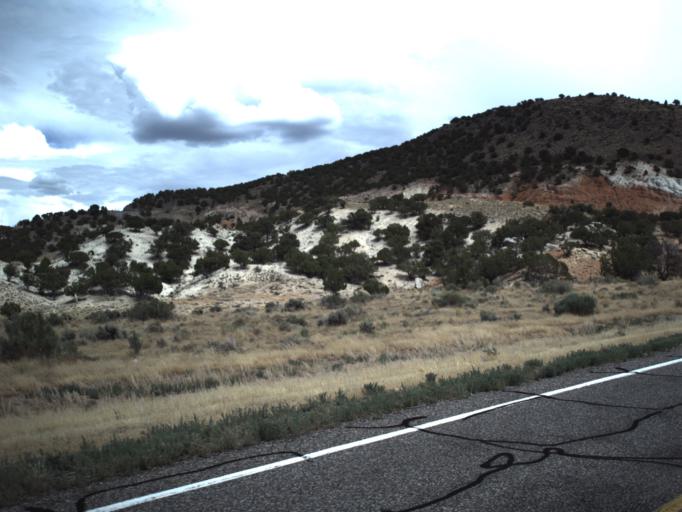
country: US
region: Utah
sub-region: Sevier County
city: Richfield
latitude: 38.7755
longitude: -111.9513
